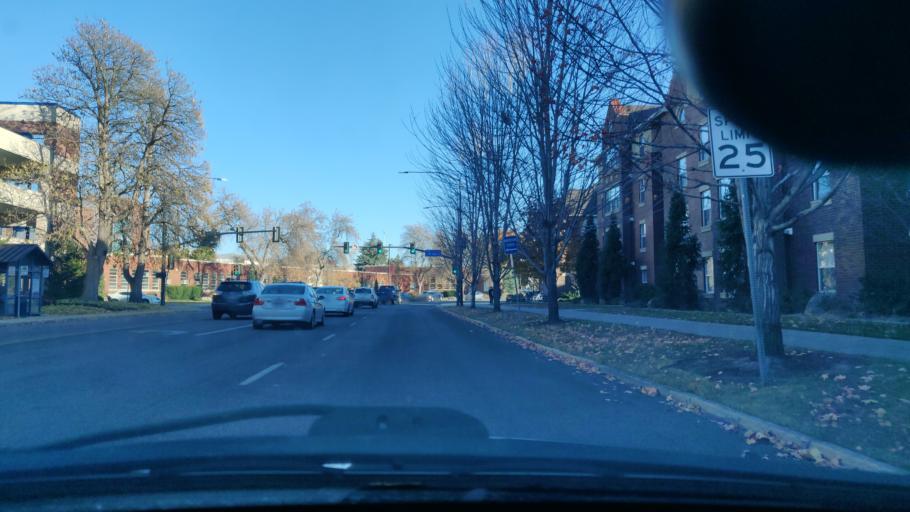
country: US
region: Idaho
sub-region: Ada County
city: Boise
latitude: 43.6047
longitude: -116.2087
